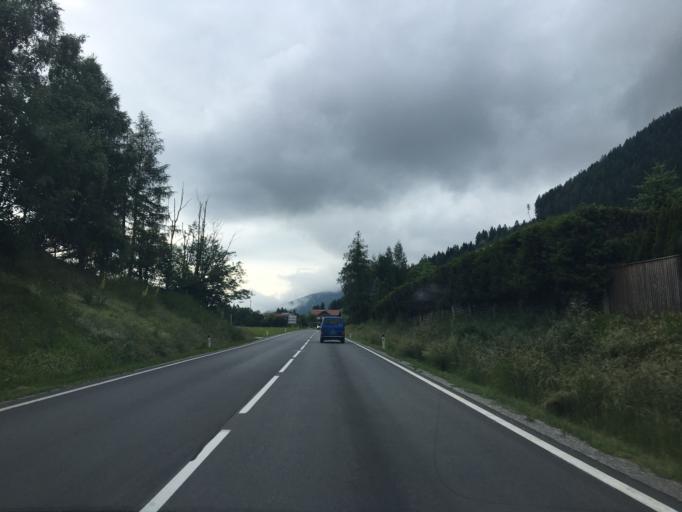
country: AT
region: Tyrol
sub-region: Politischer Bezirk Innsbruck Land
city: Mieders
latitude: 47.1747
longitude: 11.3890
